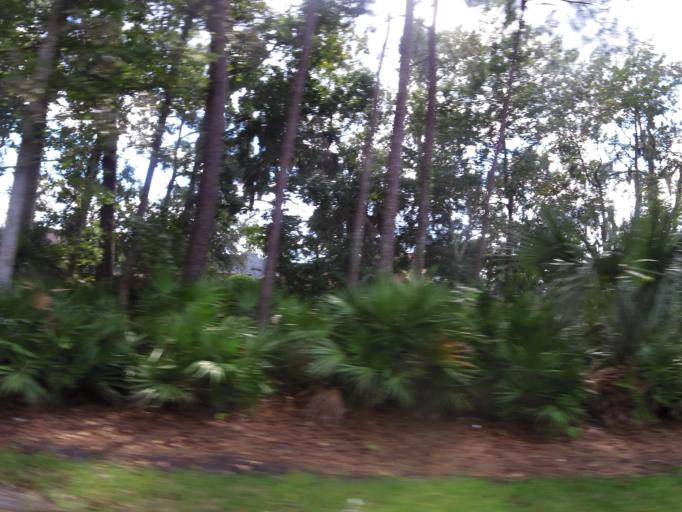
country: US
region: Florida
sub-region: Saint Johns County
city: Ponte Vedra Beach
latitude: 30.2514
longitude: -81.3998
